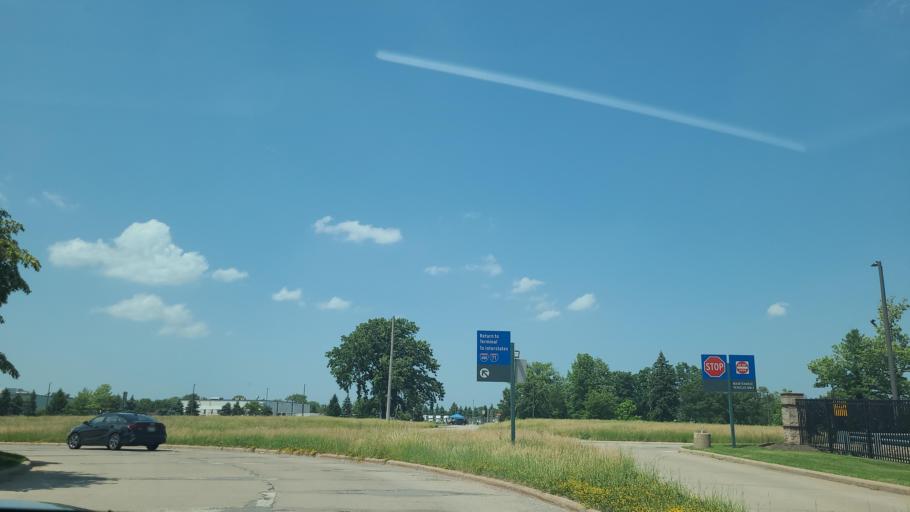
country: US
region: Ohio
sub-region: Cuyahoga County
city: Fairview Park
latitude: 41.4236
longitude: -81.8357
